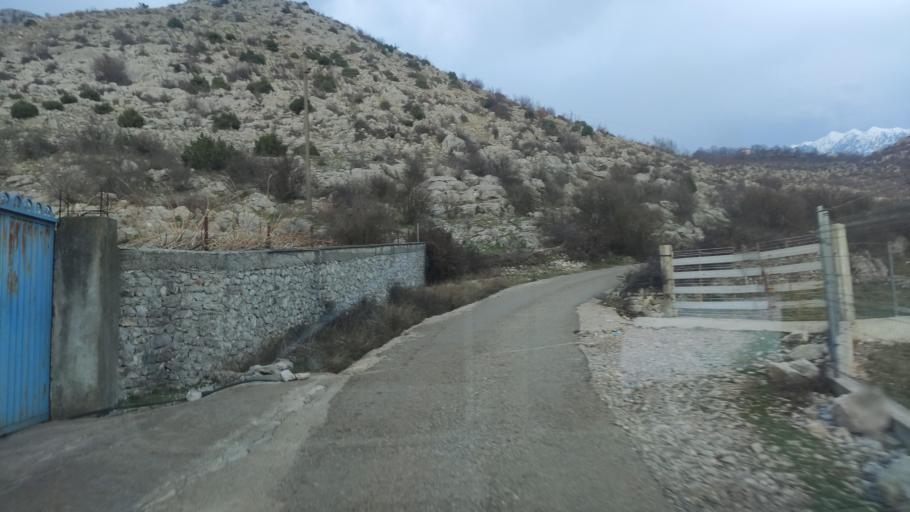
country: AL
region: Shkoder
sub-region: Rrethi i Malesia e Madhe
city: Gruemire
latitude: 42.2386
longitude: 19.5311
